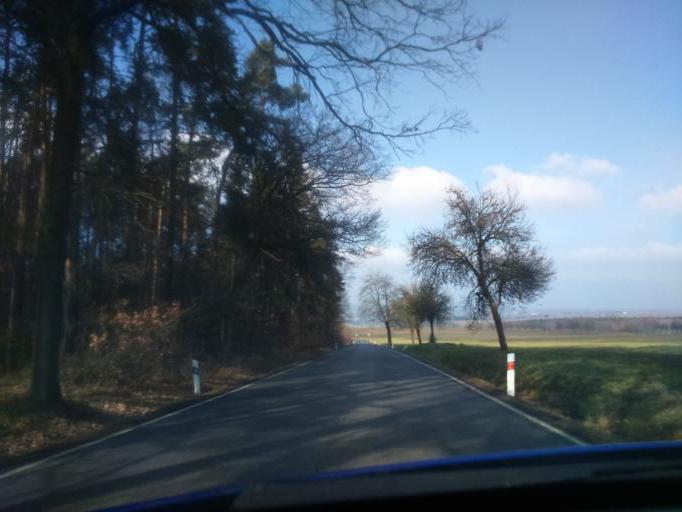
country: CZ
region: Plzensky
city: Horsovsky Tyn
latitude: 49.4948
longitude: 12.9458
